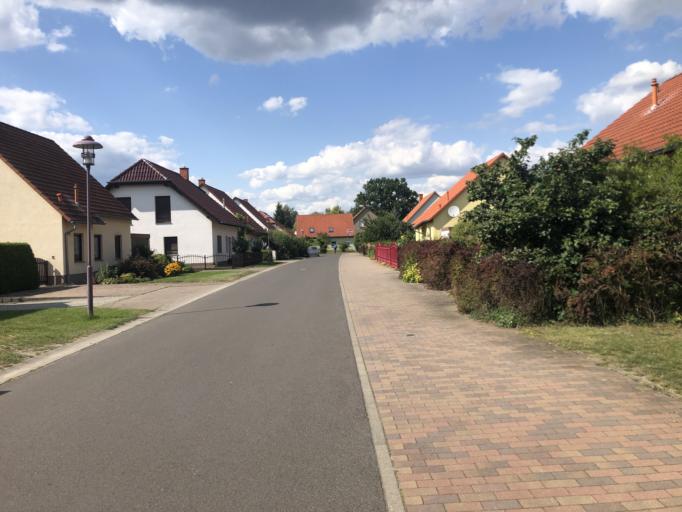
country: DE
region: Brandenburg
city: Mullrose
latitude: 52.2472
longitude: 14.4122
